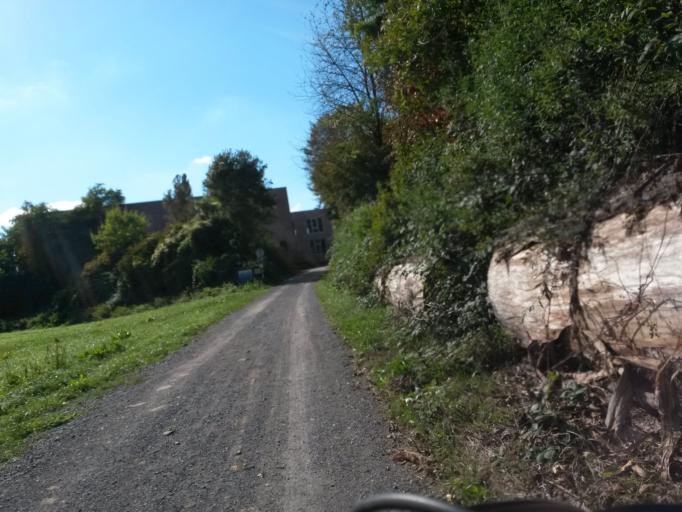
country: DE
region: Baden-Wuerttemberg
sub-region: Regierungsbezirk Stuttgart
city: Oberriexingen
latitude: 48.9322
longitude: 9.0355
